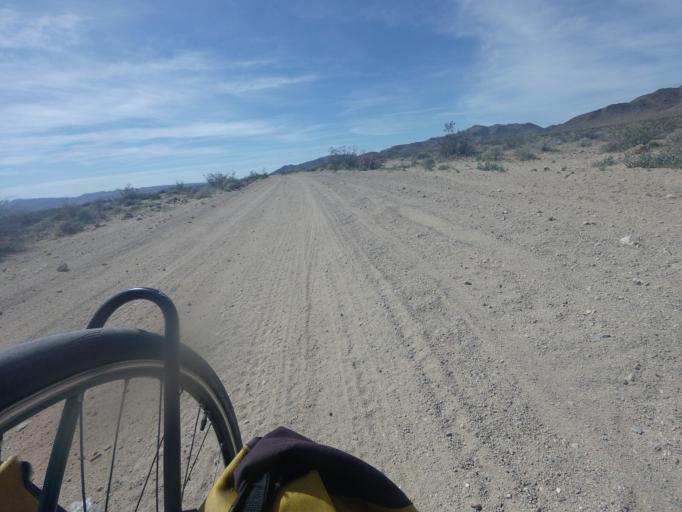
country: US
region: California
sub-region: San Bernardino County
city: Searles Valley
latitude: 35.5734
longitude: -117.4375
